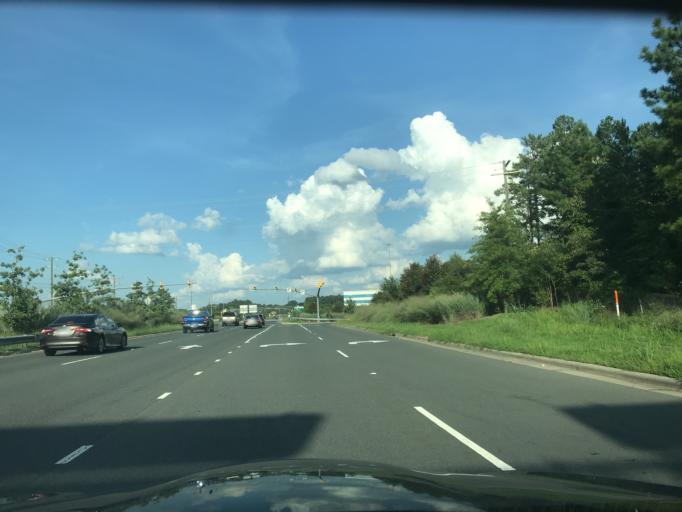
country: US
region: North Carolina
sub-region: Wake County
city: Morrisville
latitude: 35.8761
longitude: -78.8689
